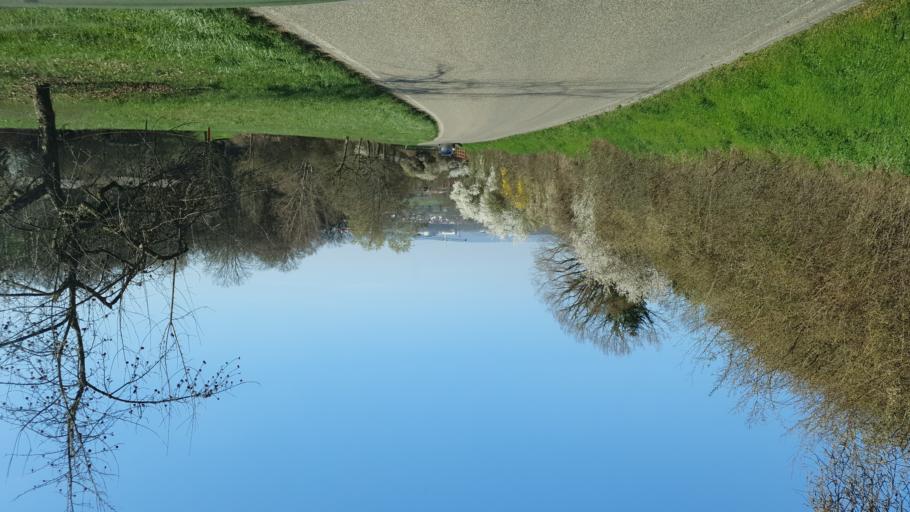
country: DE
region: Baden-Wuerttemberg
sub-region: Regierungsbezirk Stuttgart
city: Offenau
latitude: 49.2611
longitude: 9.1436
